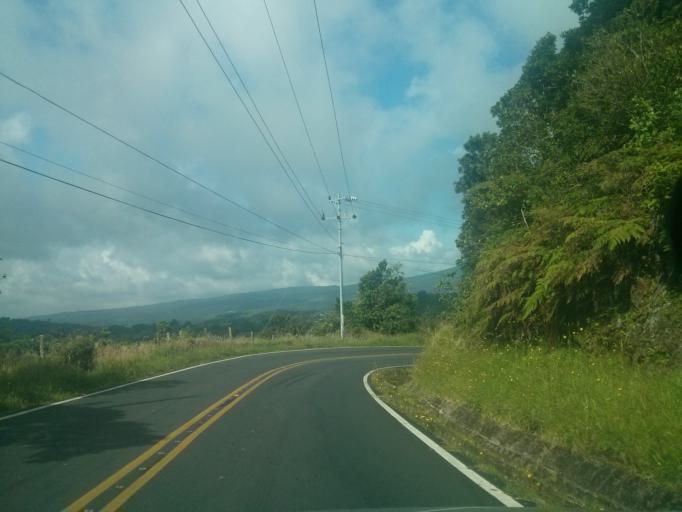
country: CR
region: Alajuela
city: Sabanilla
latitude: 10.1675
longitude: -84.1866
